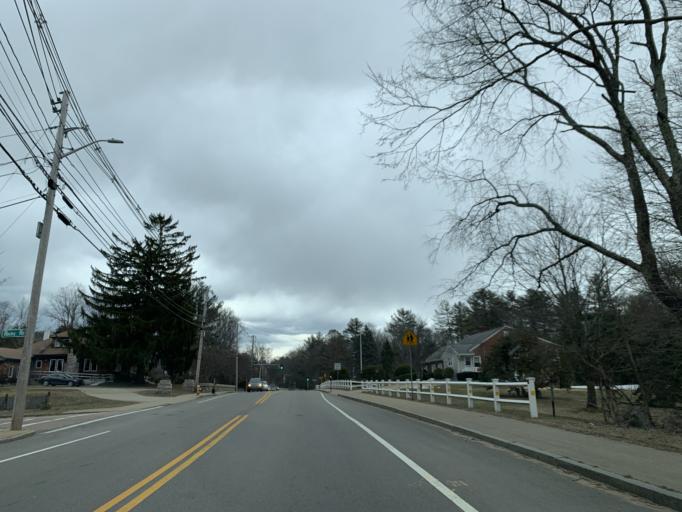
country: US
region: Massachusetts
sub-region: Norfolk County
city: Franklin
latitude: 42.0556
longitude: -71.4240
